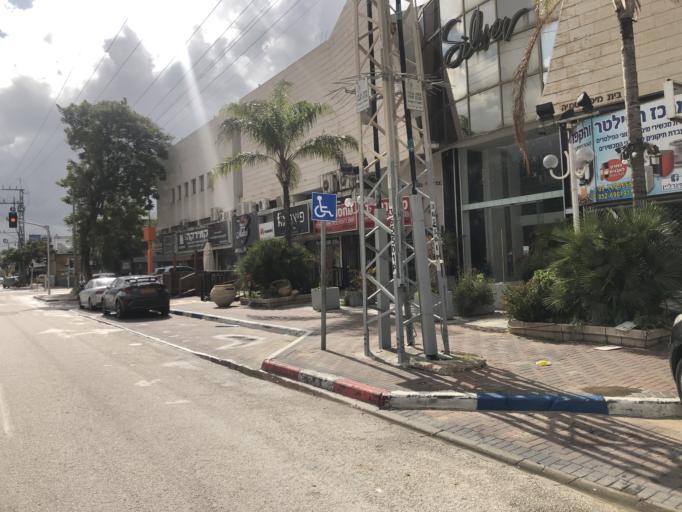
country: IL
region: Central District
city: Bet Yizhaq
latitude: 32.3209
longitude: 34.8743
